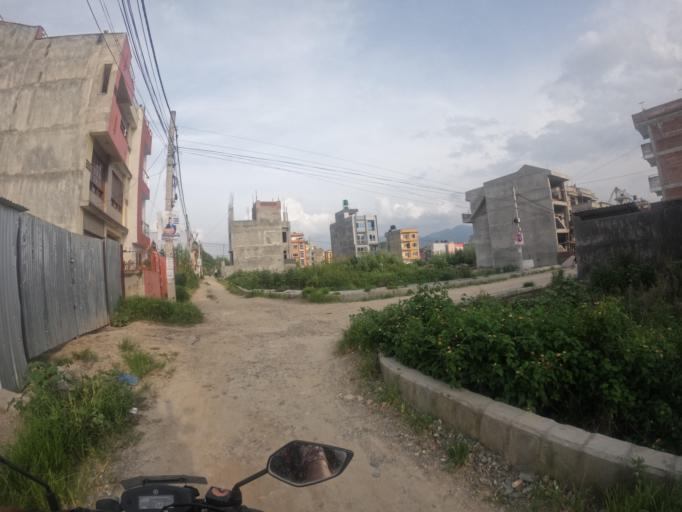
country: NP
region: Central Region
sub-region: Bagmati Zone
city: Bhaktapur
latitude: 27.6761
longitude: 85.3898
